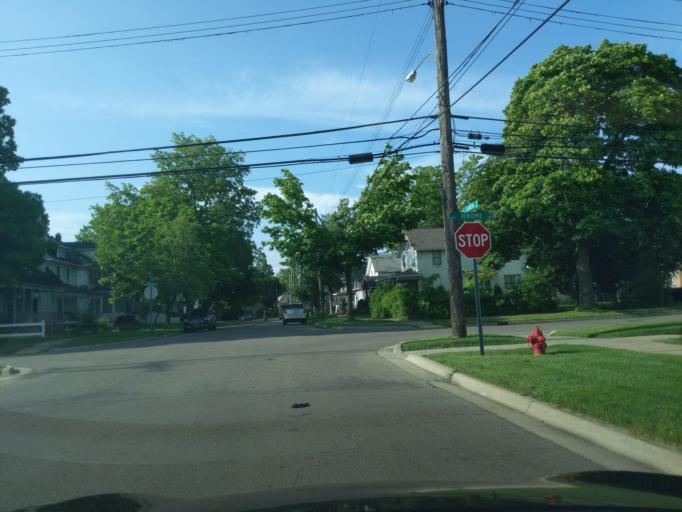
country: US
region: Michigan
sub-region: Ingham County
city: Lansing
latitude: 42.7345
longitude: -84.5395
